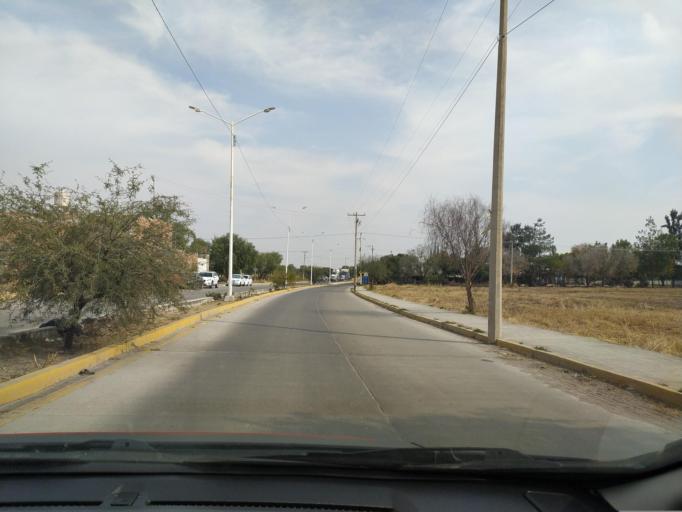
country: MX
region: Guanajuato
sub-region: San Francisco del Rincon
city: Fraccionamiento la Mezquitera
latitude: 21.0179
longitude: -101.8351
